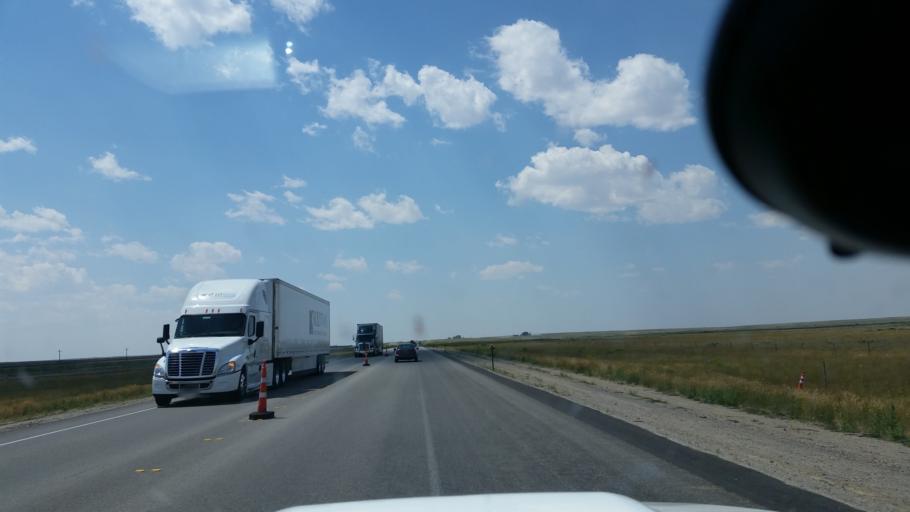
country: US
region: Wyoming
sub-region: Carbon County
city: Rawlins
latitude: 41.7222
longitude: -107.7569
